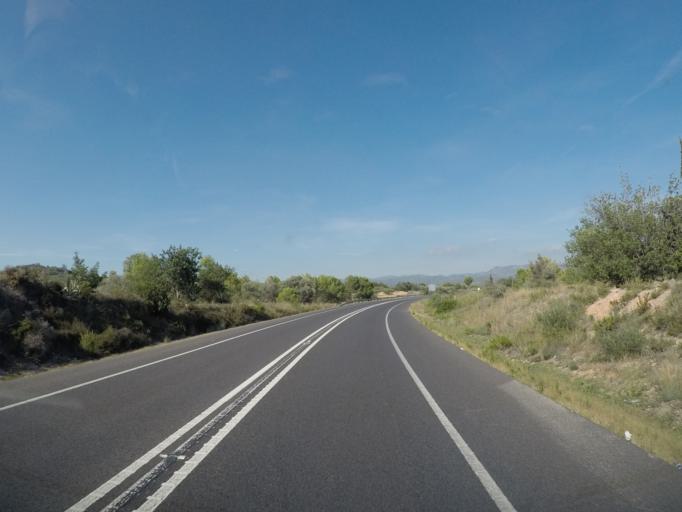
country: ES
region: Catalonia
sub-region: Provincia de Tarragona
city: El Perello
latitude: 40.8864
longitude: 0.7192
